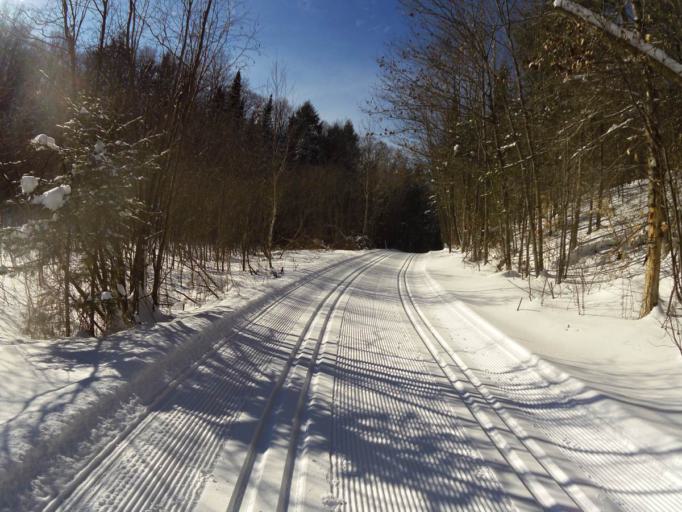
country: CA
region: Quebec
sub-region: Outaouais
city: Wakefield
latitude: 45.6240
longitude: -76.0006
